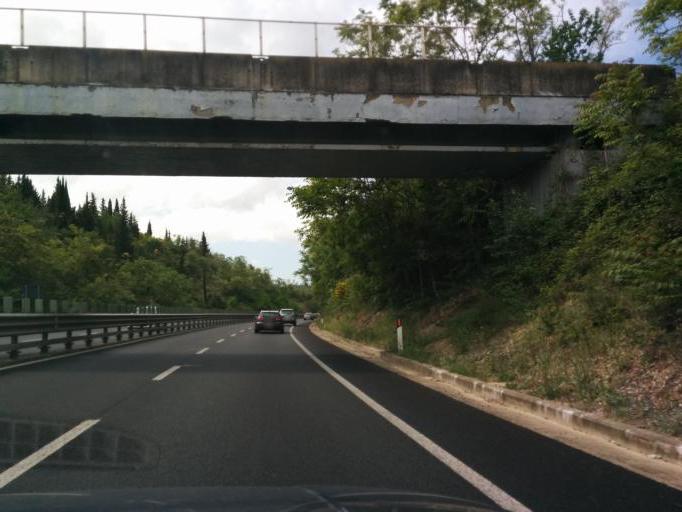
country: IT
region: Tuscany
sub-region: Province of Florence
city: Sambuca
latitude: 43.5384
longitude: 11.2205
